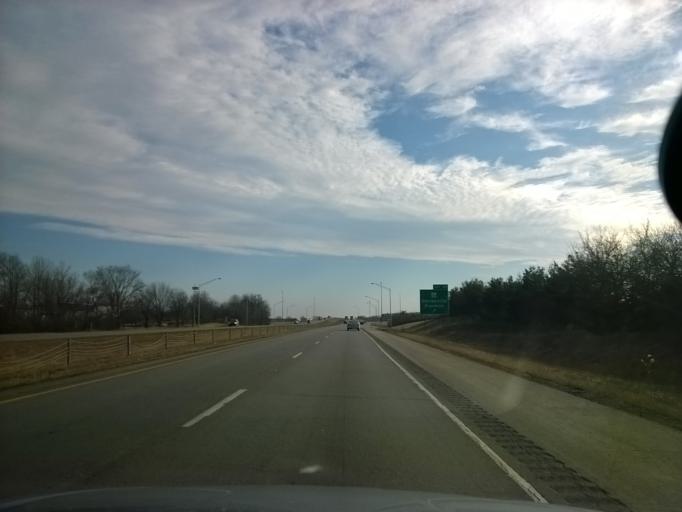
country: US
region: Indiana
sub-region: Johnson County
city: Franklin
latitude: 39.4903
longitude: -86.0161
